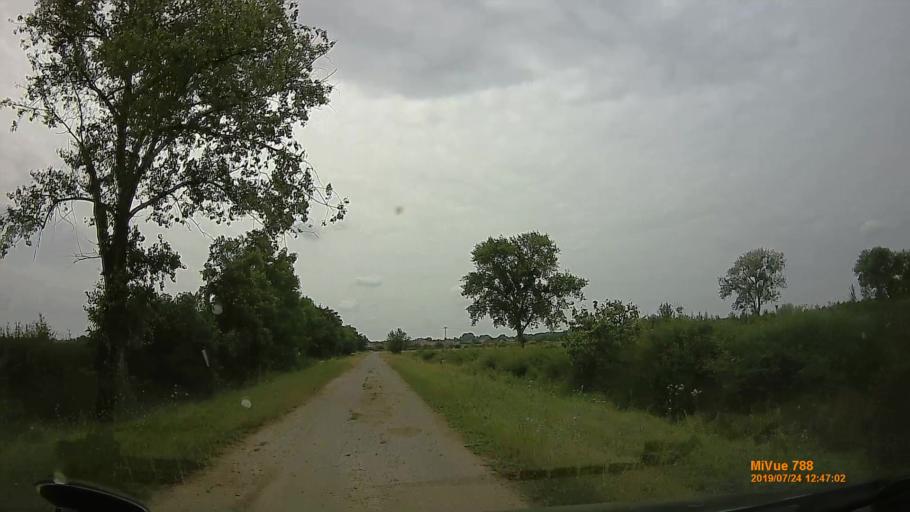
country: HU
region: Szabolcs-Szatmar-Bereg
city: Aranyosapati
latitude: 48.1955
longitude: 22.3194
